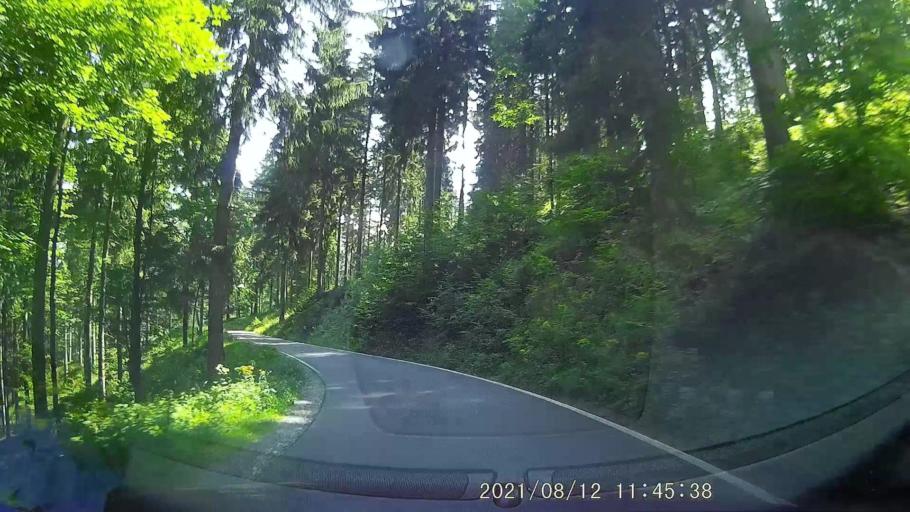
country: PL
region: Lower Silesian Voivodeship
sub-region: Powiat klodzki
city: Stronie Slaskie
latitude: 50.2510
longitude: 16.8412
